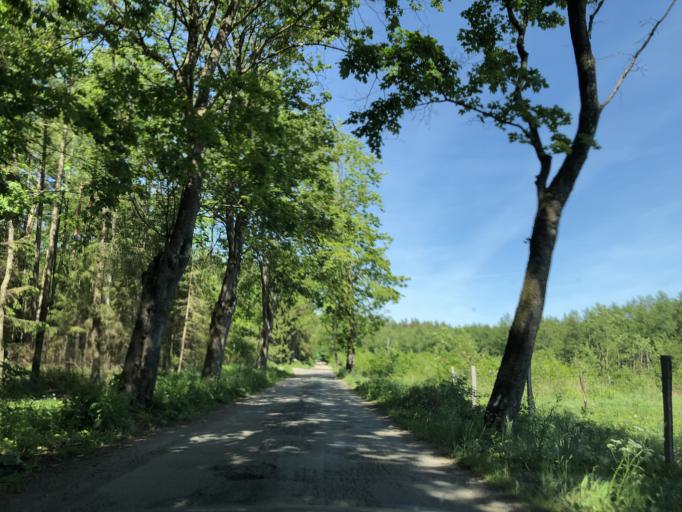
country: PL
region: West Pomeranian Voivodeship
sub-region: Powiat kolobrzeski
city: Goscino
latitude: 54.0230
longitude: 15.7387
